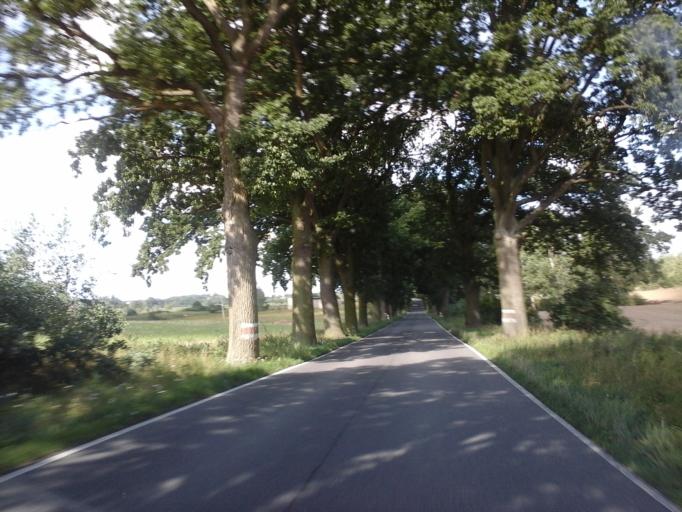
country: PL
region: West Pomeranian Voivodeship
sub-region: Powiat stargardzki
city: Dolice
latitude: 53.1963
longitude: 15.2273
